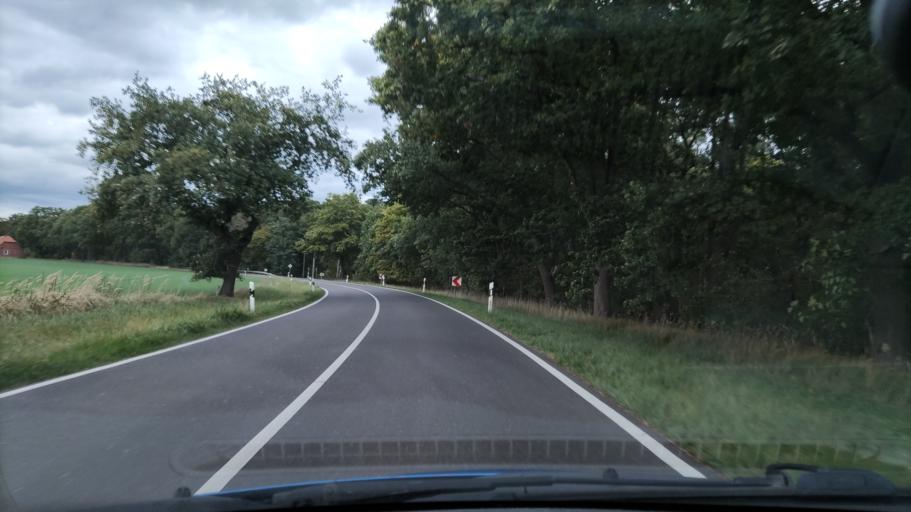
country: DE
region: Mecklenburg-Vorpommern
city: Lubtheen
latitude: 53.3523
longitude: 10.9610
